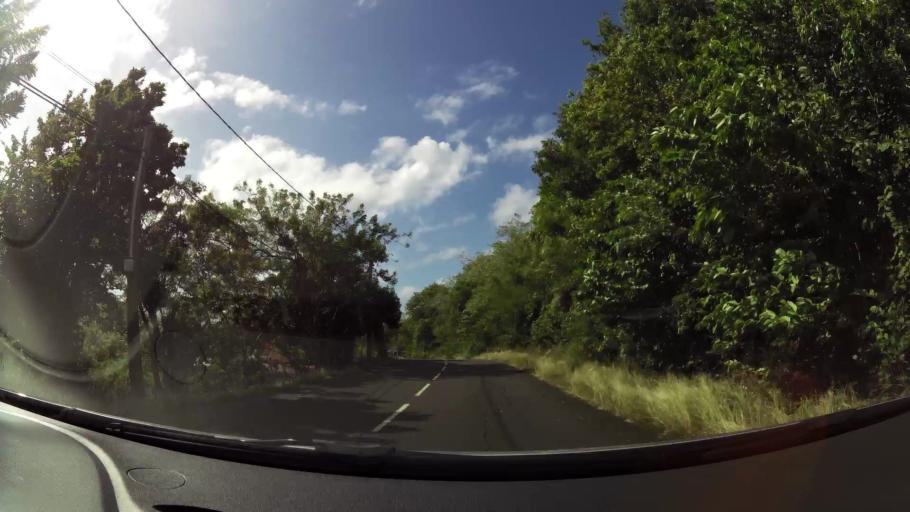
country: MQ
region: Martinique
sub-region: Martinique
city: Le Marin
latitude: 14.4247
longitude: -60.8751
